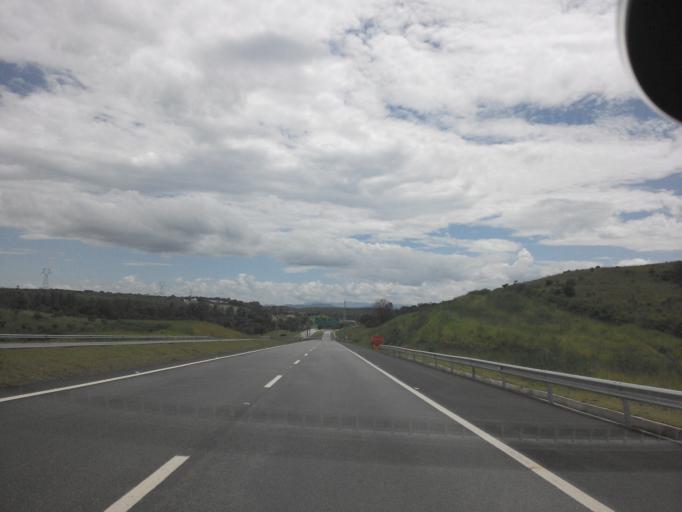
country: BR
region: Sao Paulo
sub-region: Taubate
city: Taubate
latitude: -23.1020
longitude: -45.5985
